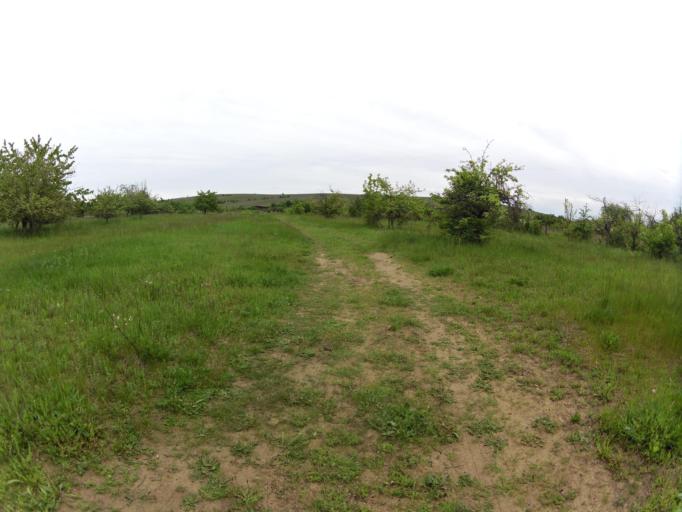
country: DE
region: Bavaria
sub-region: Regierungsbezirk Unterfranken
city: Nordheim
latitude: 49.8487
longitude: 10.1700
